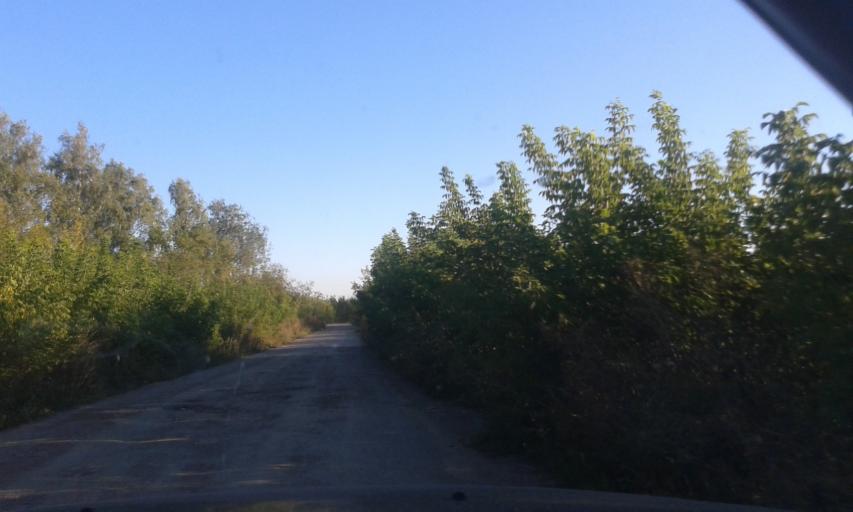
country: RU
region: Tula
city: Krapivna
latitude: 54.1329
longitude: 37.1571
